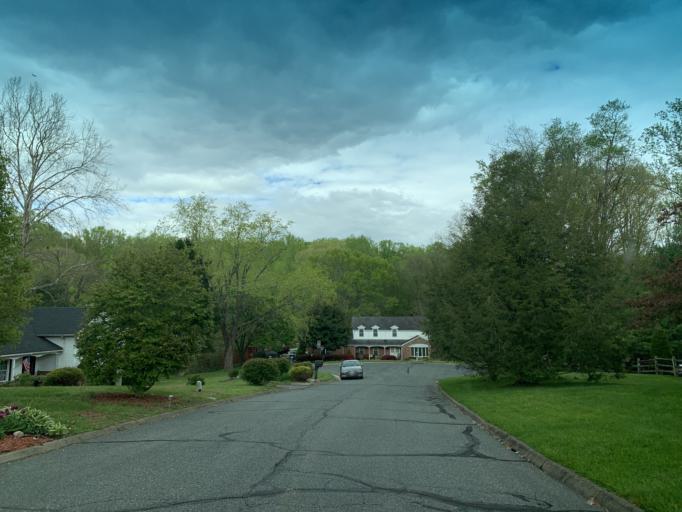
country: US
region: Maryland
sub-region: Harford County
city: Pleasant Hills
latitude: 39.4977
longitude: -76.3599
